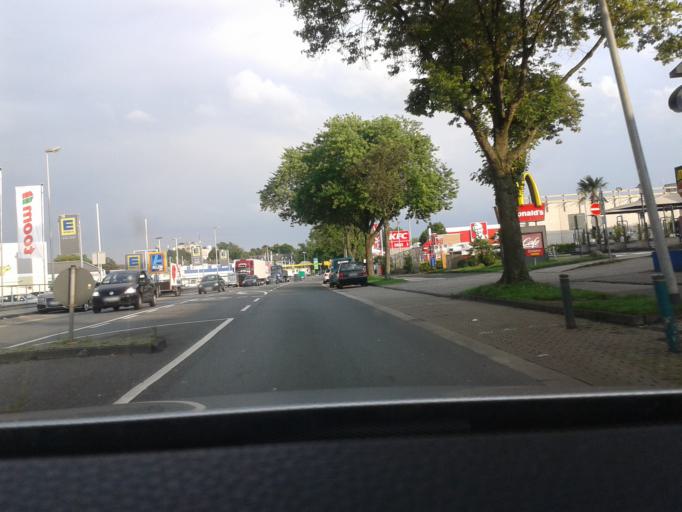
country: DE
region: North Rhine-Westphalia
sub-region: Regierungsbezirk Dusseldorf
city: Hochfeld
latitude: 51.4195
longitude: 6.7077
